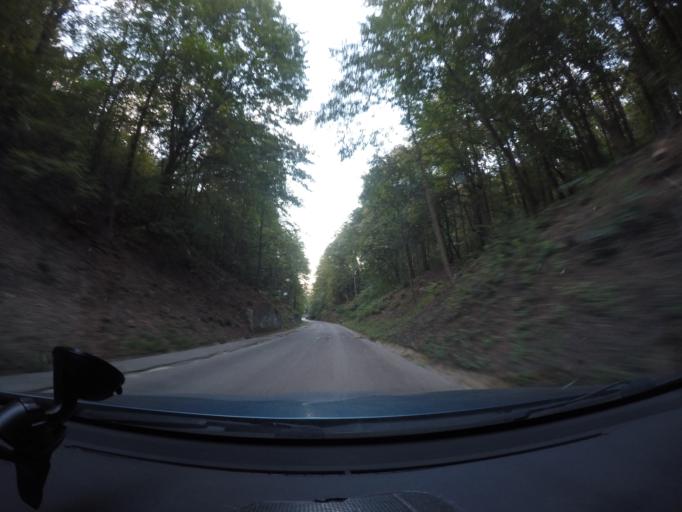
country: SK
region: Trenciansky
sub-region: Okres Trencin
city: Trencin
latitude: 48.8877
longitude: 18.0488
